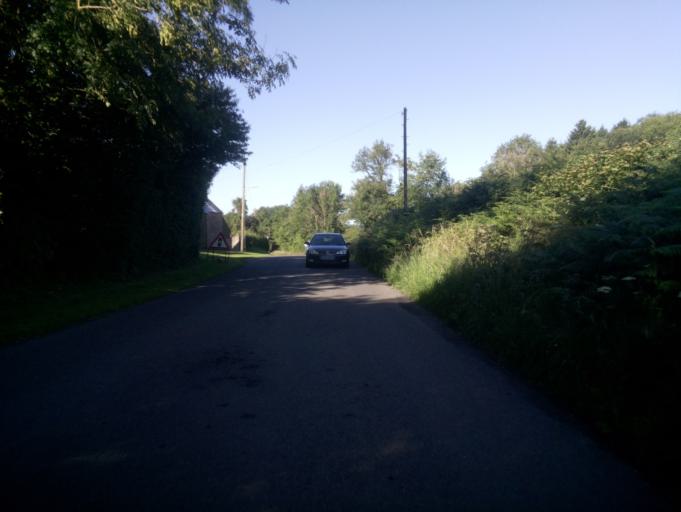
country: GB
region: England
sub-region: Gloucestershire
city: Coleford
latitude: 51.7968
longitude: -2.6347
